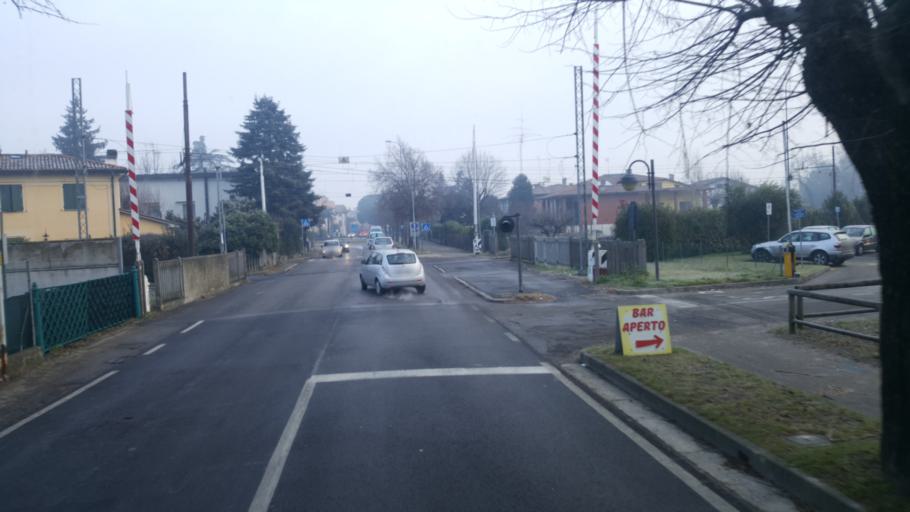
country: IT
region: Emilia-Romagna
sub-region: Provincia di Ravenna
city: Bagnacavallo
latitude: 44.4116
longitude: 11.9715
